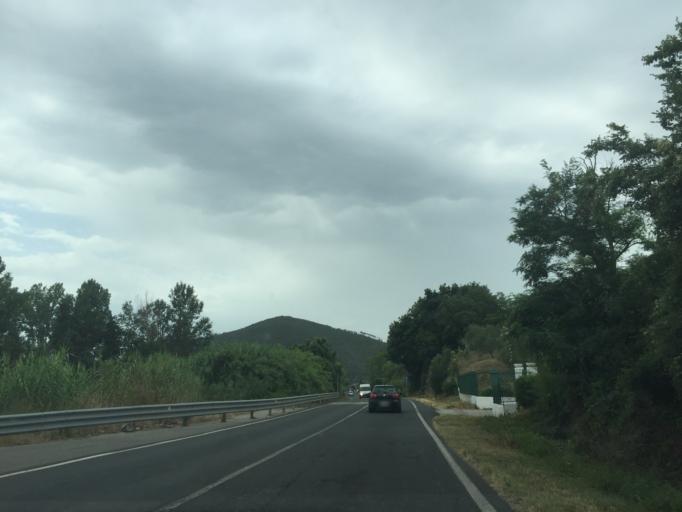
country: IT
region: Tuscany
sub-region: Province of Pisa
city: Asciano
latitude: 43.7433
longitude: 10.4676
